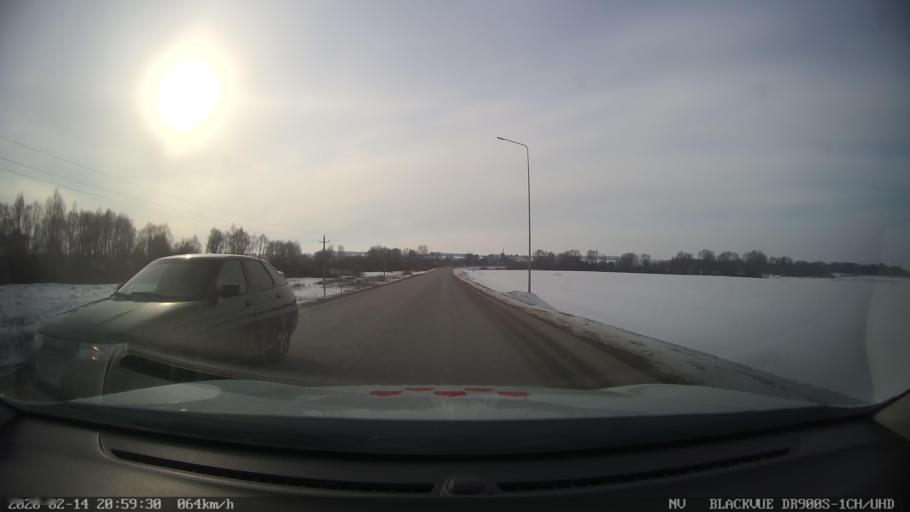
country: RU
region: Tatarstan
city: Kuybyshevskiy Zaton
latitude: 55.1781
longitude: 49.2375
